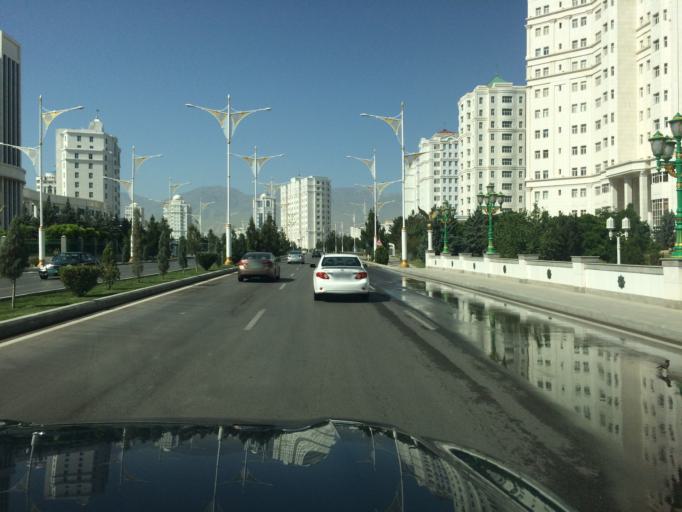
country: TM
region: Ahal
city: Ashgabat
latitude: 37.9123
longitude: 58.3683
